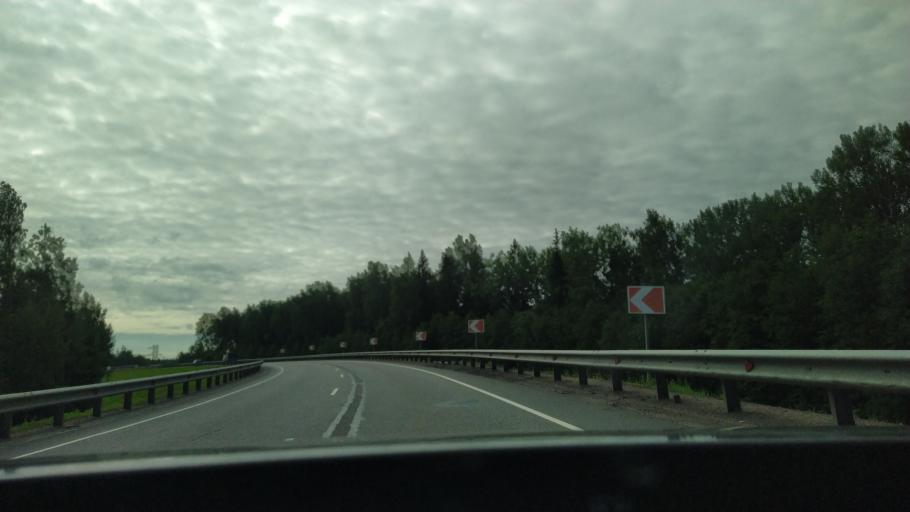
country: RU
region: Leningrad
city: Ul'yanovka
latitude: 59.5947
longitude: 30.7754
